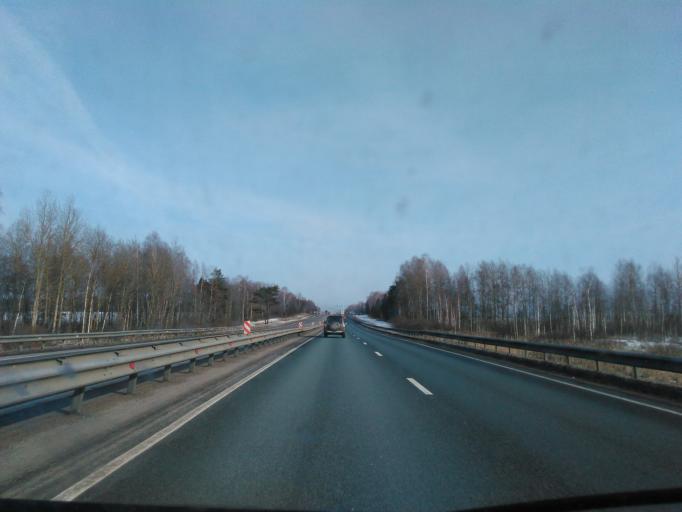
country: RU
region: Smolensk
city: Verkhnedneprovskiy
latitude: 55.1823
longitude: 33.5379
